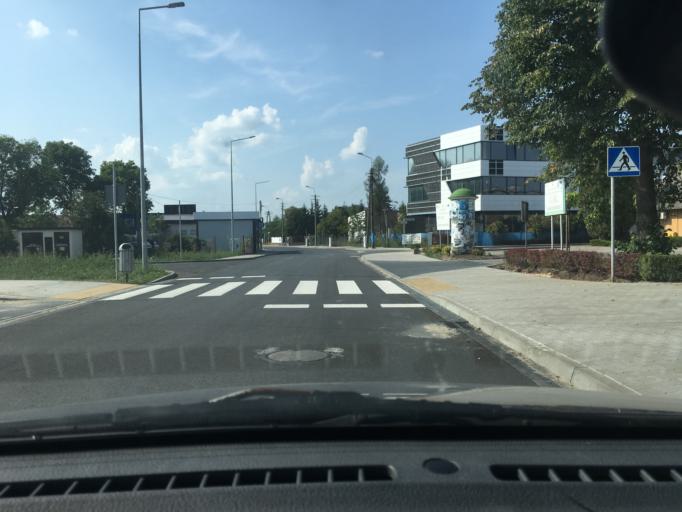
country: PL
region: Masovian Voivodeship
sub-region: Powiat piaseczynski
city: Lesznowola
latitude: 52.0902
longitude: 20.9365
